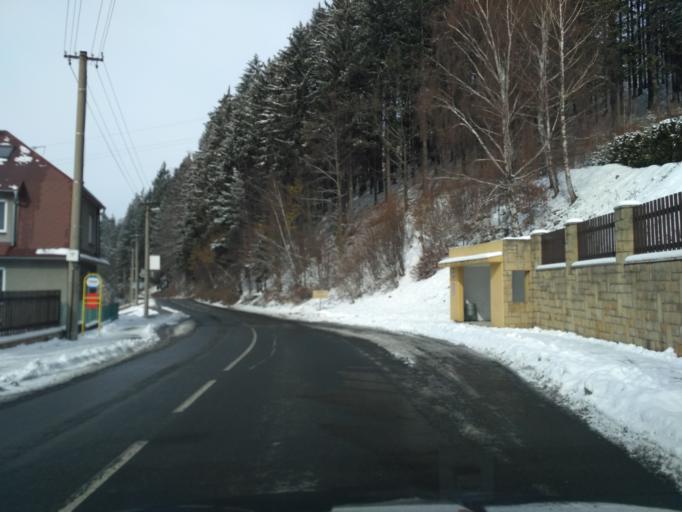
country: CZ
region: Zlin
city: Valasska Bystrice
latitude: 49.4155
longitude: 18.1092
